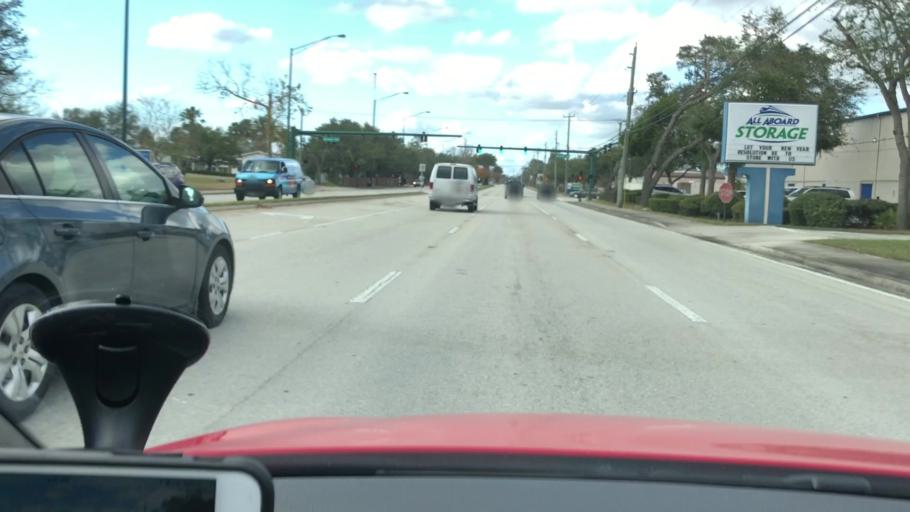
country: US
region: Florida
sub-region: Volusia County
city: Ormond Beach
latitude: 29.2657
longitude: -81.0782
